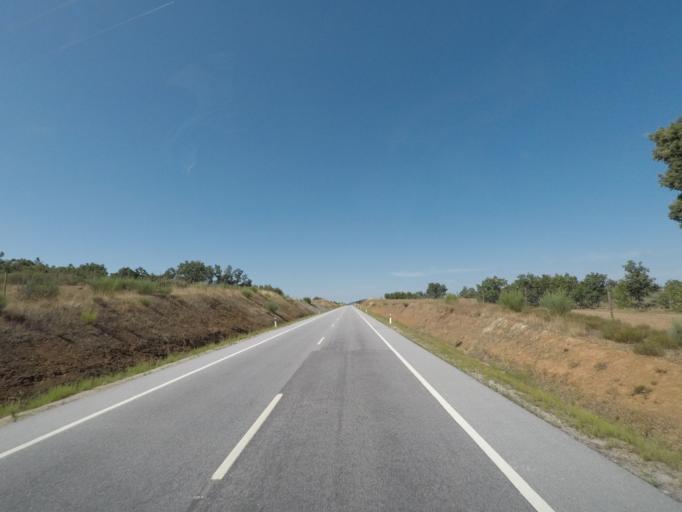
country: ES
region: Castille and Leon
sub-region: Provincia de Salamanca
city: Villarino de los Aires
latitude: 41.3623
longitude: -6.5342
